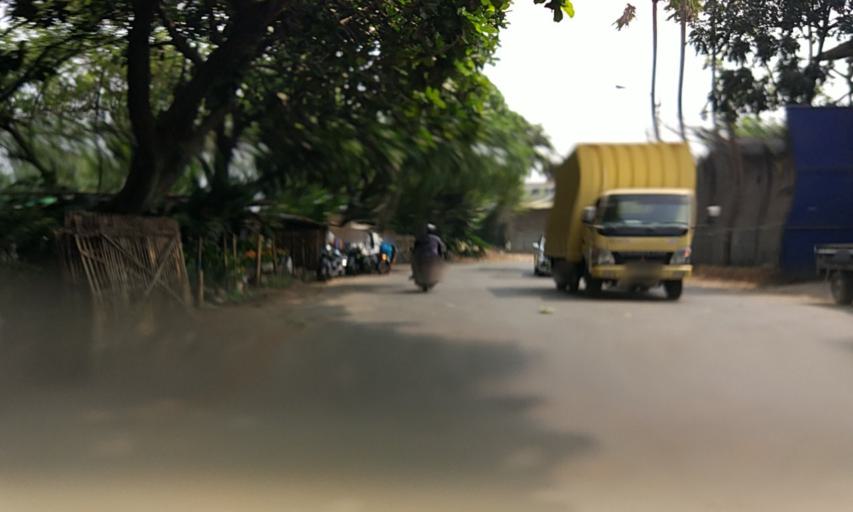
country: ID
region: West Java
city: Margahayukencana
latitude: -6.9499
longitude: 107.5623
